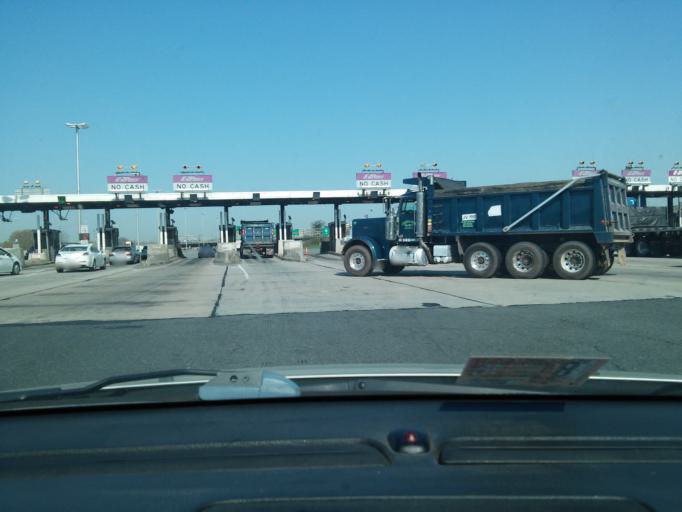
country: US
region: New Jersey
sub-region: Essex County
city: Newark
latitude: 40.7082
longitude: -74.1558
